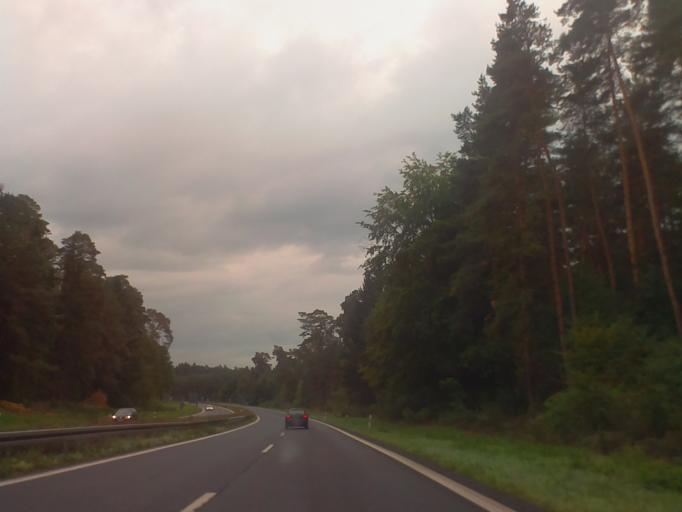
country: DE
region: Bavaria
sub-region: Regierungsbezirk Unterfranken
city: Stockstadt am Main
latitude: 49.9539
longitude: 9.0533
